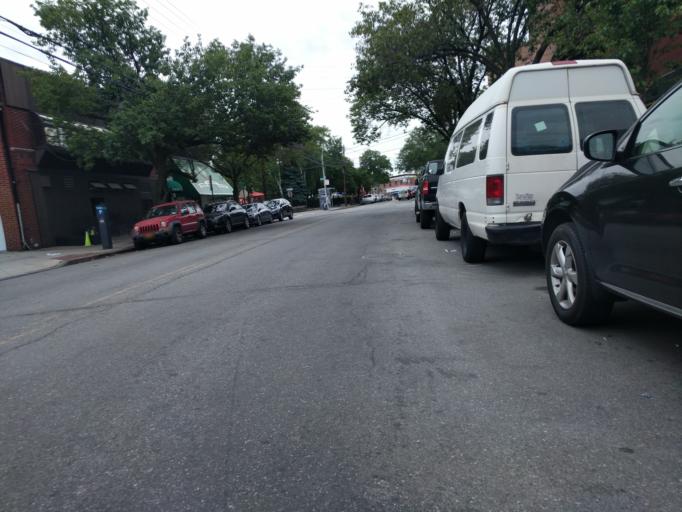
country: US
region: New York
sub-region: Queens County
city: Borough of Queens
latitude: 40.7438
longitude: -73.8567
